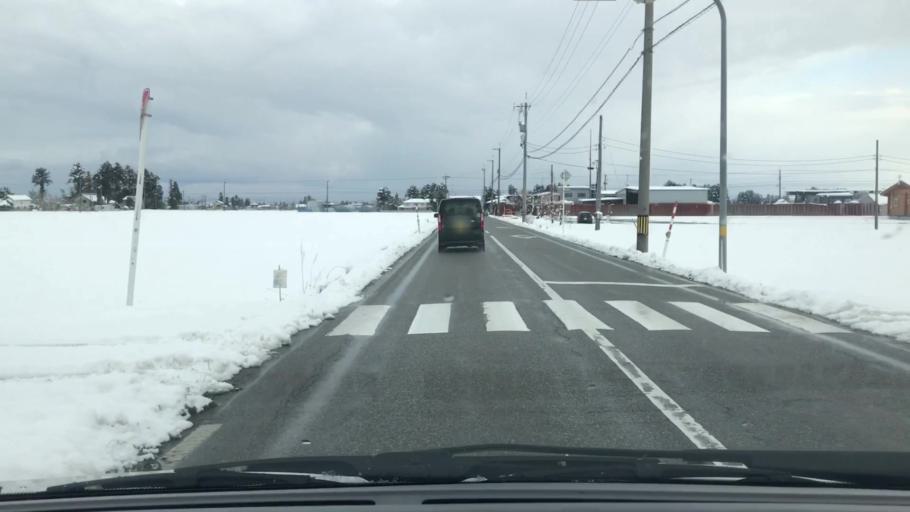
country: JP
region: Toyama
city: Kamiichi
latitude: 36.6390
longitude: 137.3285
